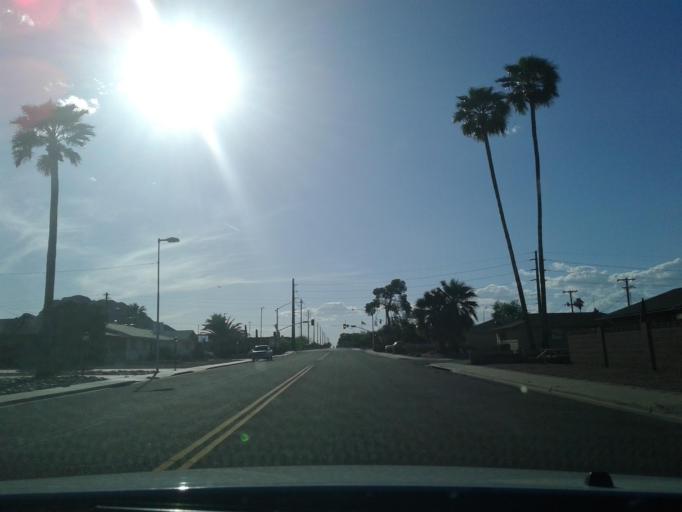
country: US
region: Arizona
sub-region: Maricopa County
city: Scottsdale
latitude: 33.4730
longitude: -111.9418
